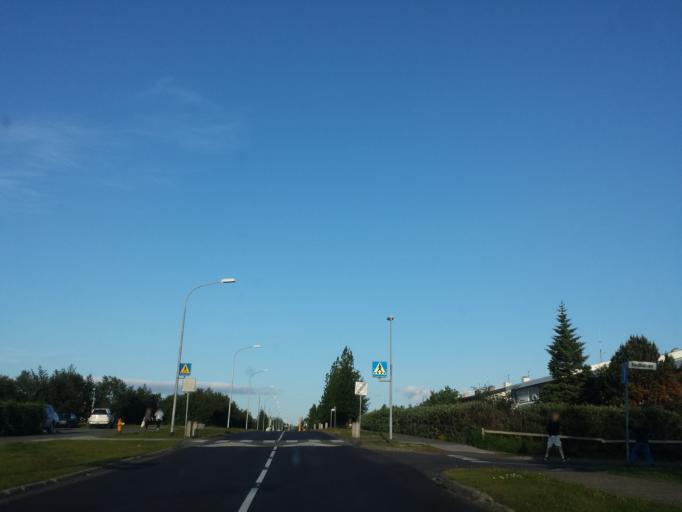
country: IS
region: Capital Region
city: Reykjavik
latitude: 64.1161
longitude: -21.7960
